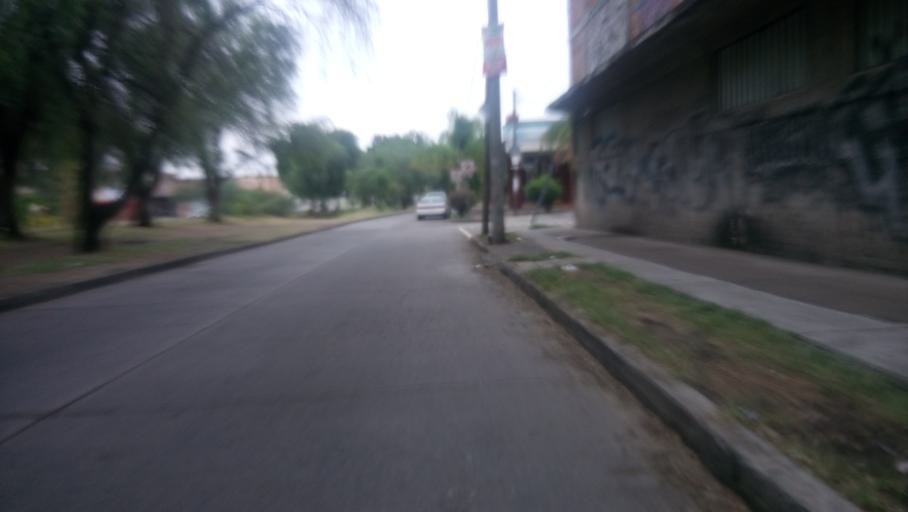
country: MX
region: Guanajuato
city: Leon
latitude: 21.1418
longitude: -101.6660
